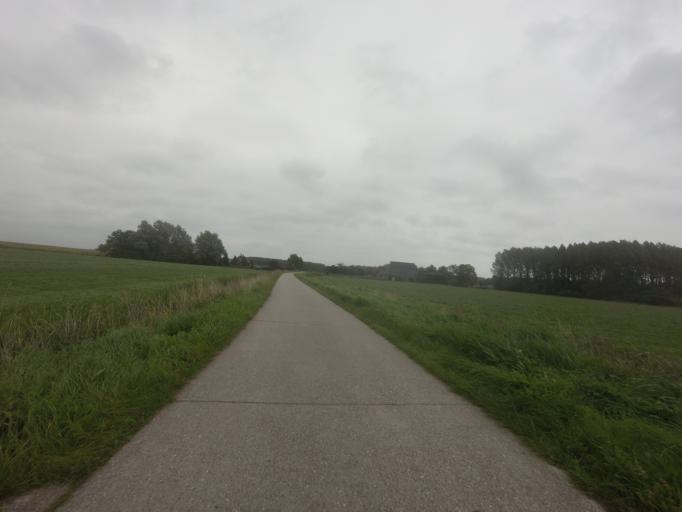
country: NL
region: Friesland
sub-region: Gemeente Leeuwarden
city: Bilgaard
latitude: 53.2269
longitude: 5.7888
